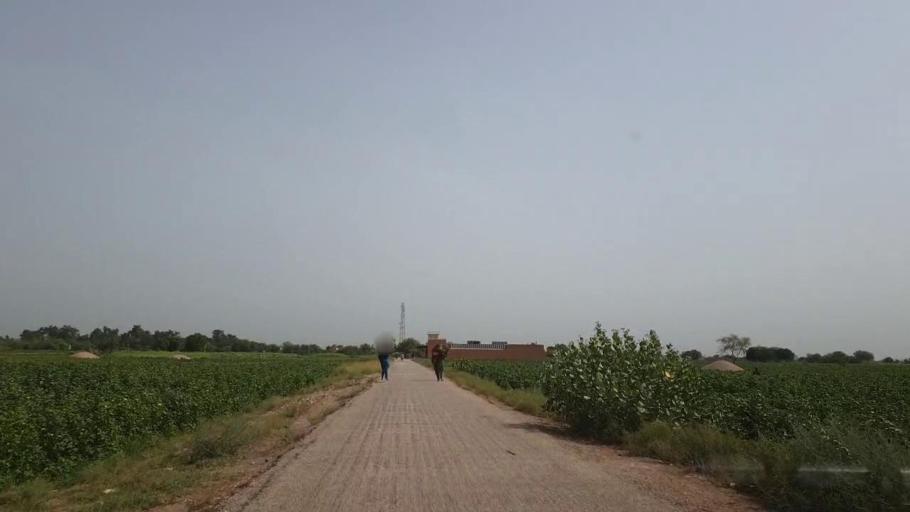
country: PK
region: Sindh
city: Sakrand
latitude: 26.1104
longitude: 68.3966
